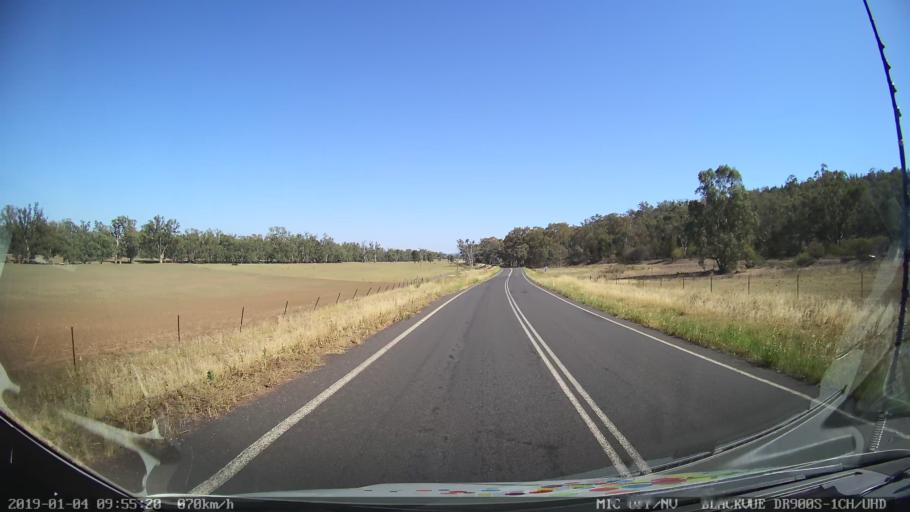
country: AU
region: New South Wales
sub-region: Cabonne
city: Canowindra
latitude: -33.5353
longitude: 148.4047
